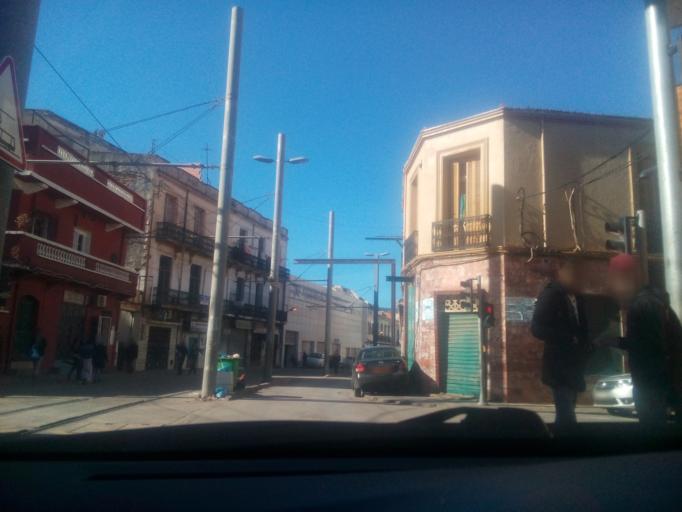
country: DZ
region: Oran
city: Oran
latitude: 35.6985
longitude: -0.6333
